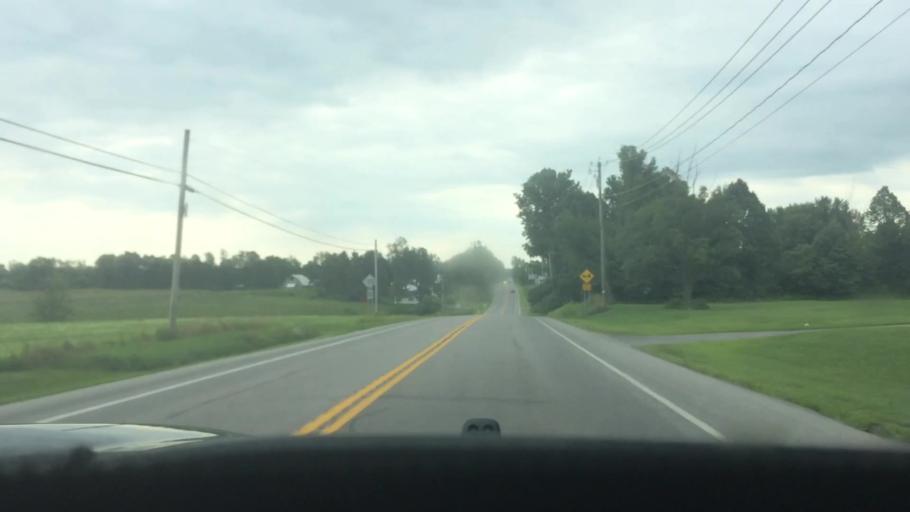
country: US
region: New York
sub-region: St. Lawrence County
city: Ogdensburg
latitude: 44.6127
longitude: -75.4002
